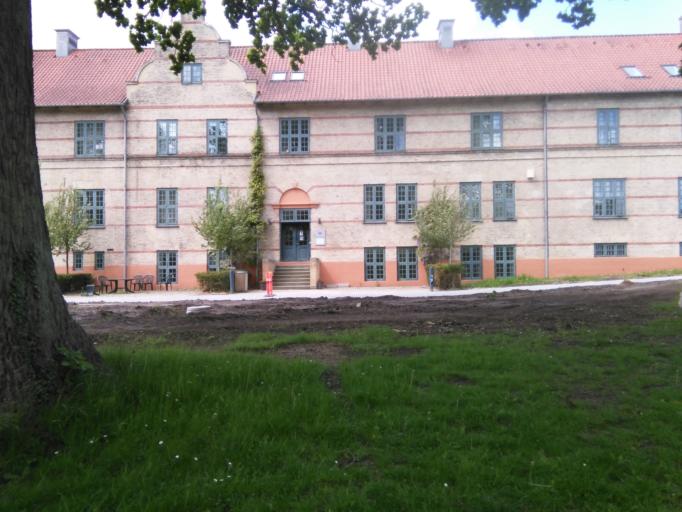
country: DK
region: Central Jutland
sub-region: Arhus Kommune
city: Arhus
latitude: 56.1862
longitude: 10.2333
